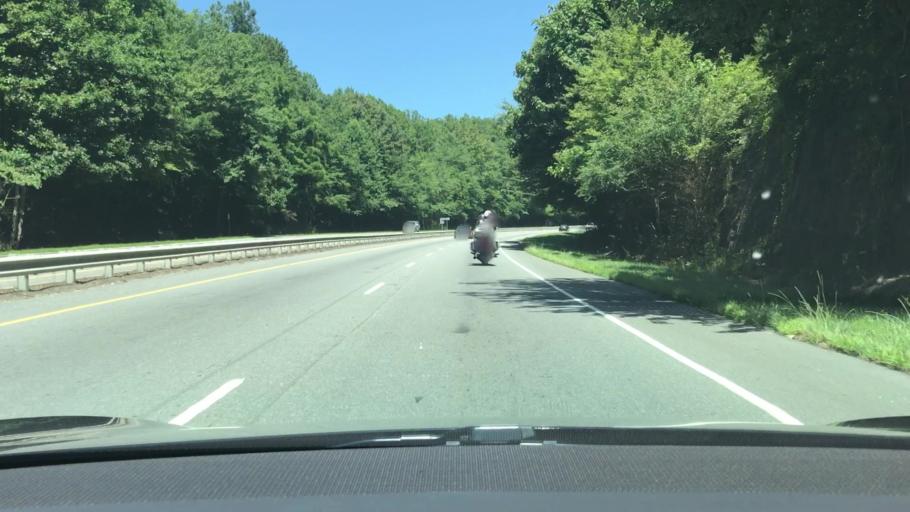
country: US
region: North Carolina
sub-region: Jackson County
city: Sylva
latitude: 35.3710
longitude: -83.2540
